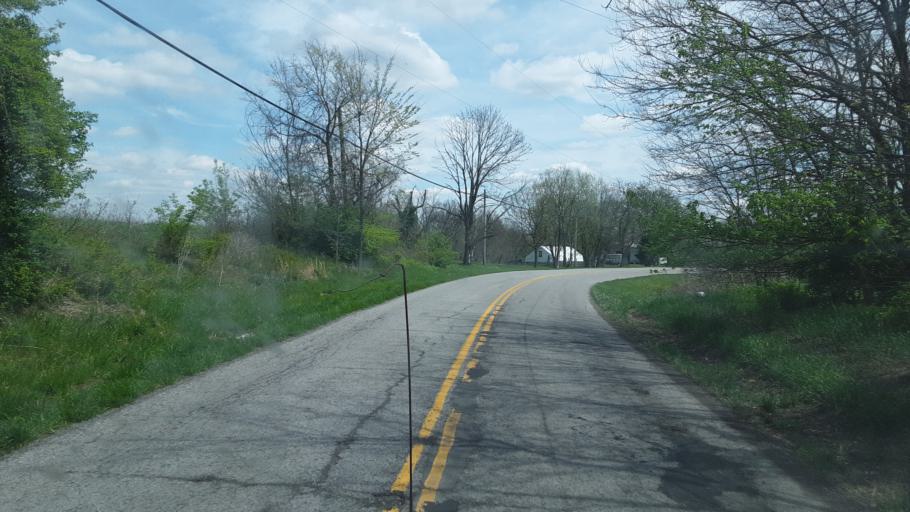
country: US
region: Kentucky
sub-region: Grant County
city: Dry Ridge
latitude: 38.6556
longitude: -84.6873
